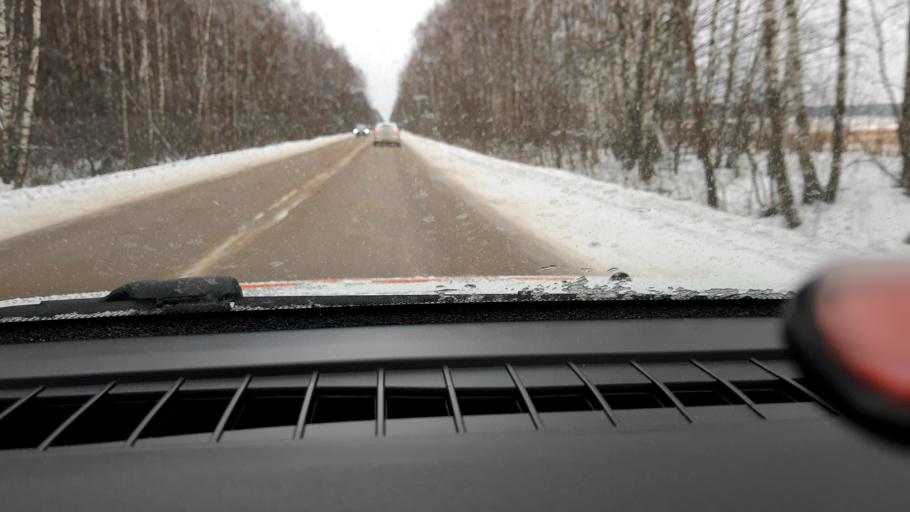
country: RU
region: Nizjnij Novgorod
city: Kstovo
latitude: 56.2968
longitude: 44.2724
